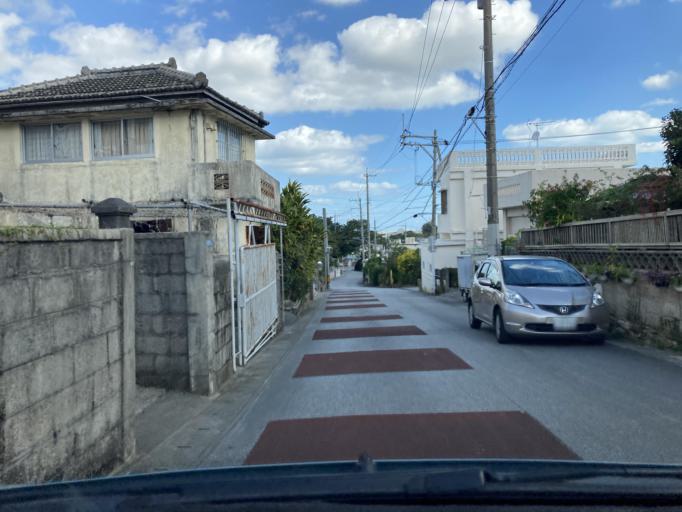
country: JP
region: Okinawa
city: Okinawa
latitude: 26.3435
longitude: 127.8050
